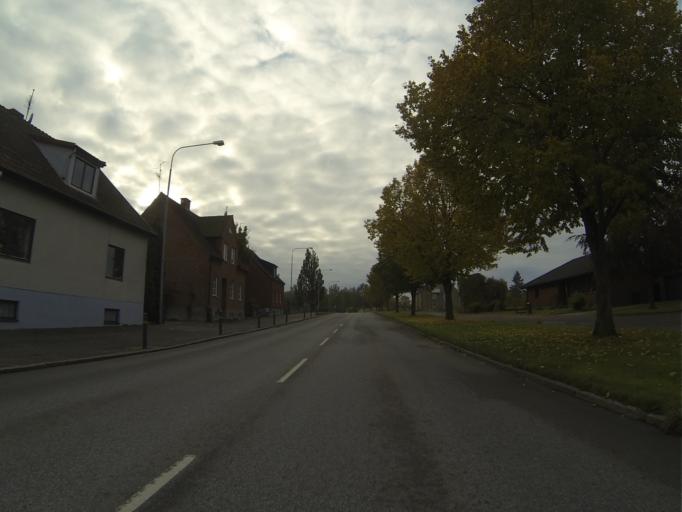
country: SE
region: Skane
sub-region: Tomelilla Kommun
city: Tomelilla
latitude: 55.5424
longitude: 13.9437
